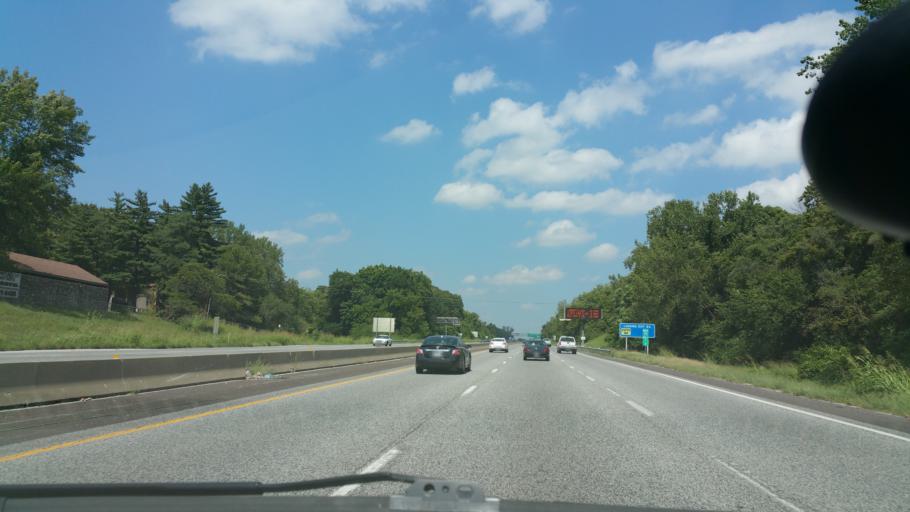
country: US
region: Missouri
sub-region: Clay County
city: North Kansas City
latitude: 39.1491
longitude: -94.5596
